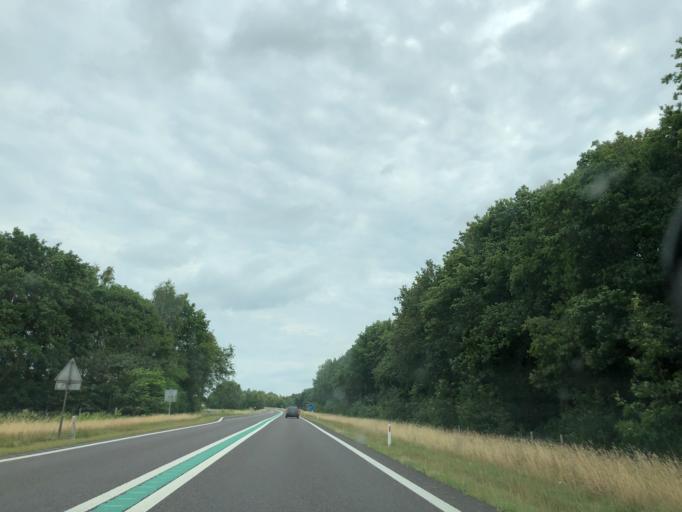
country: NL
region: Drenthe
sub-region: Gemeente Aa en Hunze
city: Anloo
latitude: 53.0539
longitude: 6.7091
